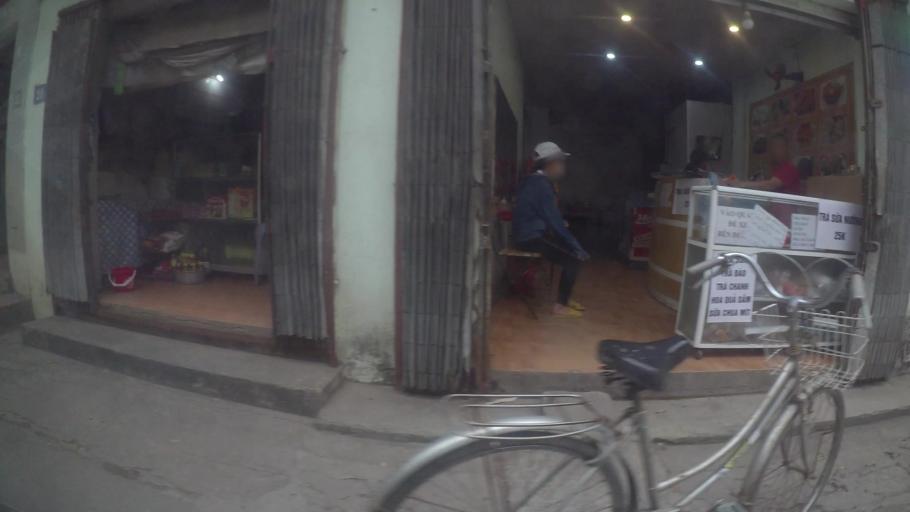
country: VN
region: Ha Noi
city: Cau Dien
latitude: 21.0355
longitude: 105.7406
